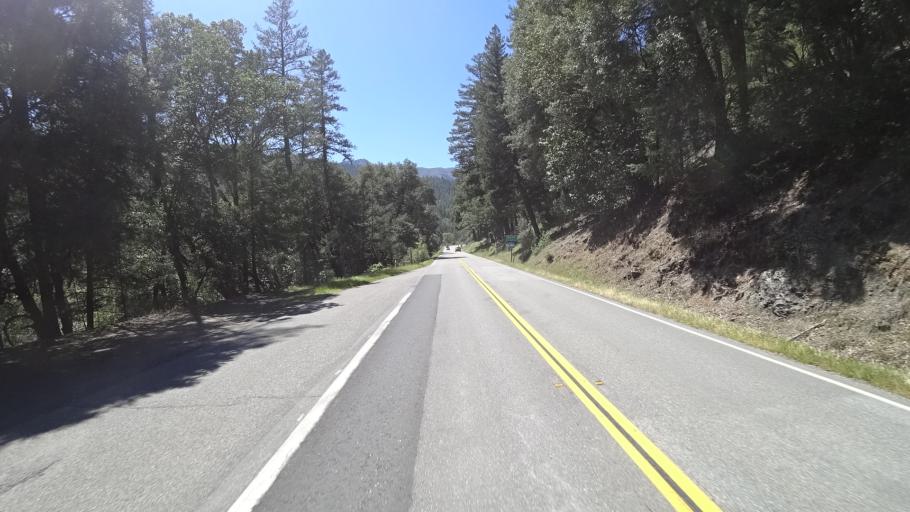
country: US
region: California
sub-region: Trinity County
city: Hayfork
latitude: 40.7418
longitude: -123.2607
